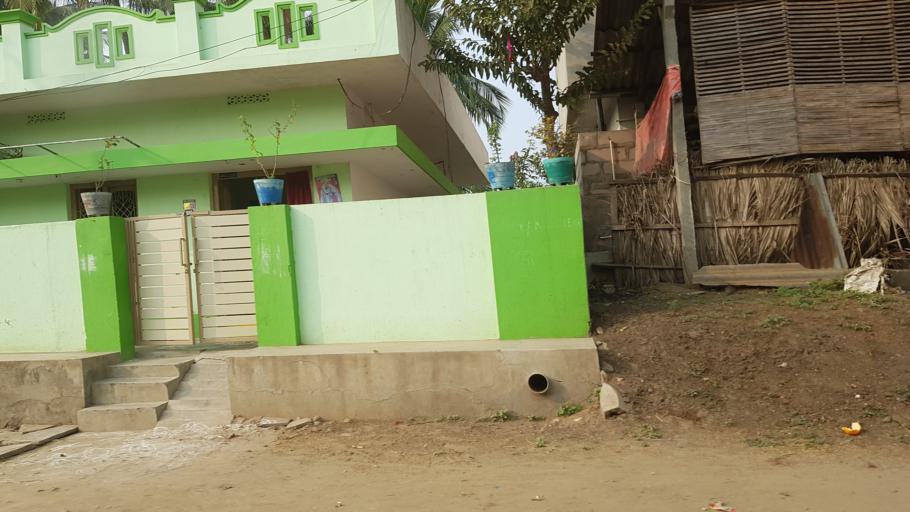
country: IN
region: Andhra Pradesh
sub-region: West Godavari
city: Akividu
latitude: 16.5363
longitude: 81.4055
